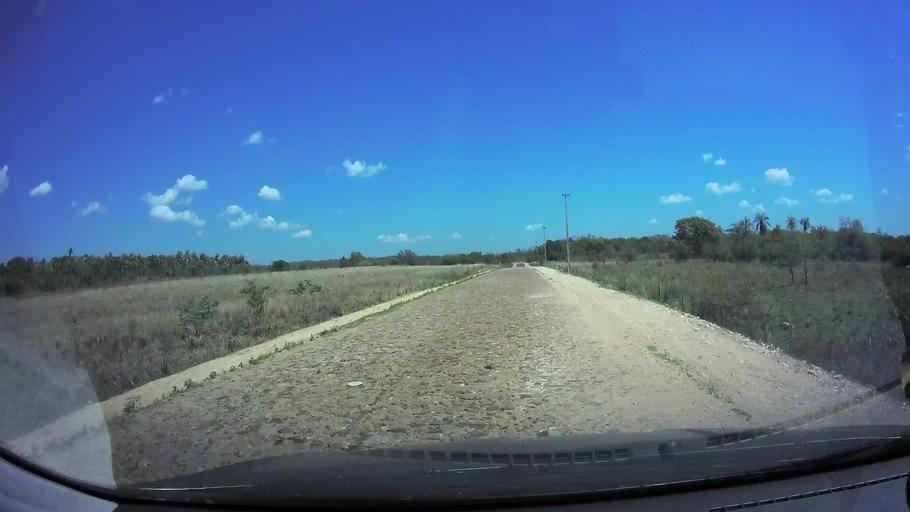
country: PY
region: Cordillera
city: Emboscada
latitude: -25.1433
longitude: -57.2612
